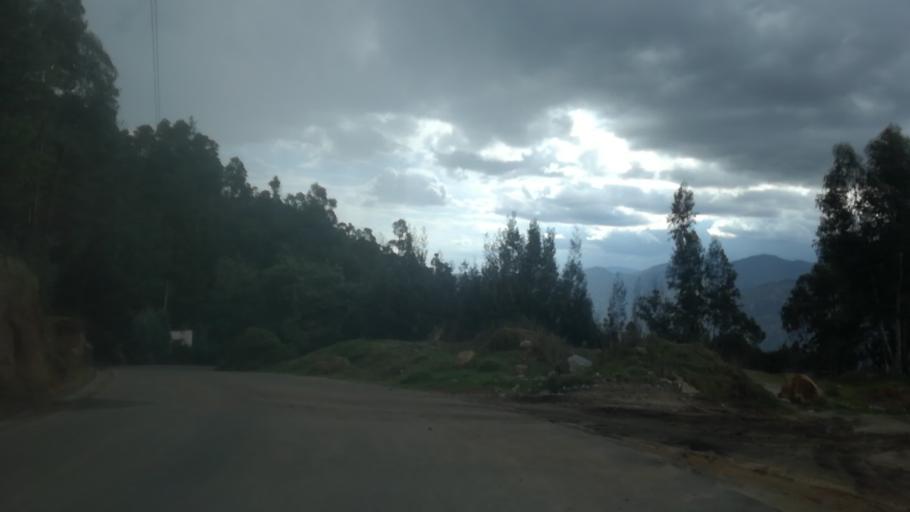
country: CO
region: Boyaca
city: Socha Viejo
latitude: 5.9968
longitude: -72.6967
